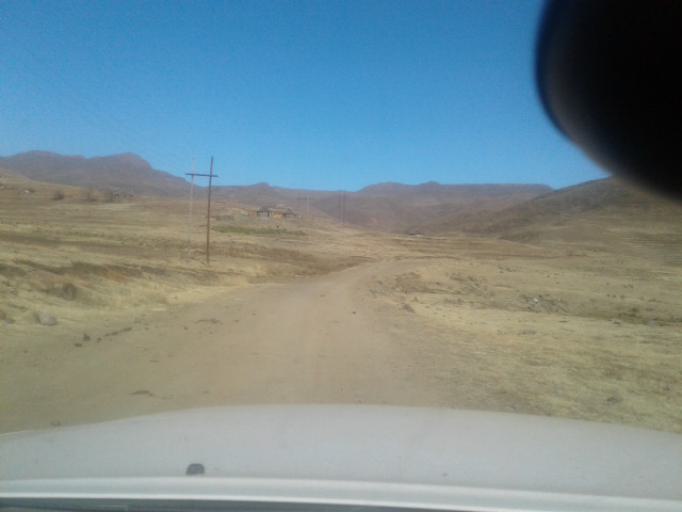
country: LS
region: Maseru
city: Nako
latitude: -29.3804
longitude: 28.0140
